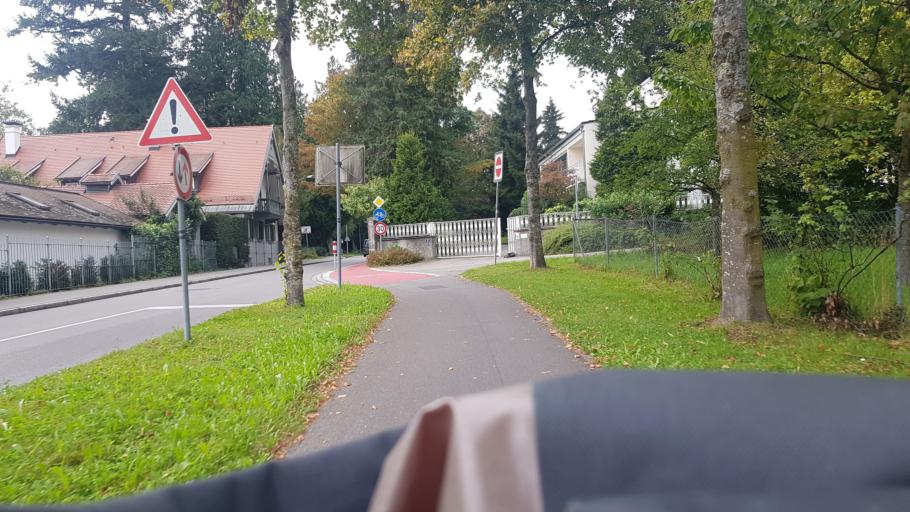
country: DE
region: Bavaria
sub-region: Swabia
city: Bodolz
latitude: 47.5587
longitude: 9.6749
